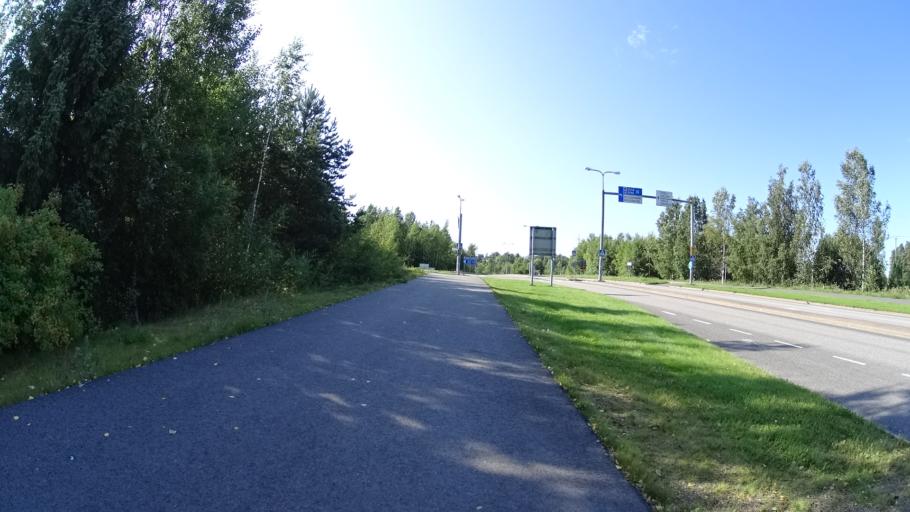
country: FI
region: Uusimaa
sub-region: Helsinki
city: Kauniainen
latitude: 60.2534
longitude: 24.7111
